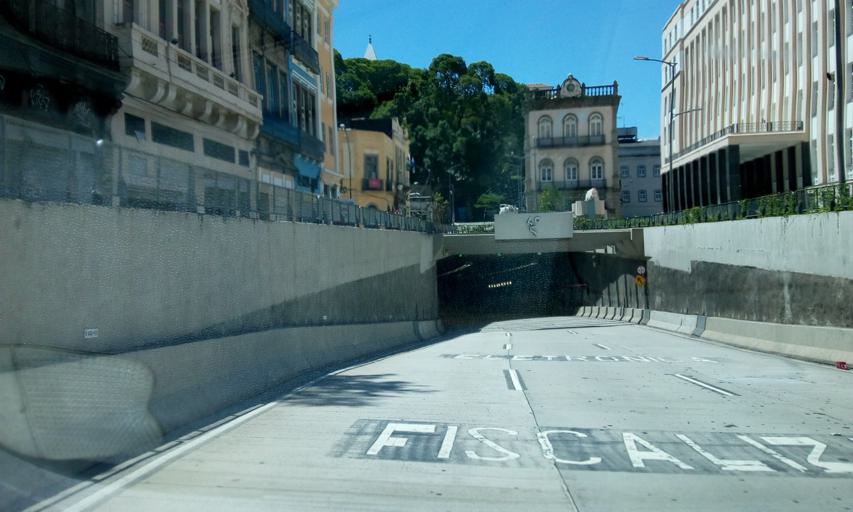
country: BR
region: Rio de Janeiro
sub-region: Rio De Janeiro
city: Rio de Janeiro
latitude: -22.8987
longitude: -43.1773
